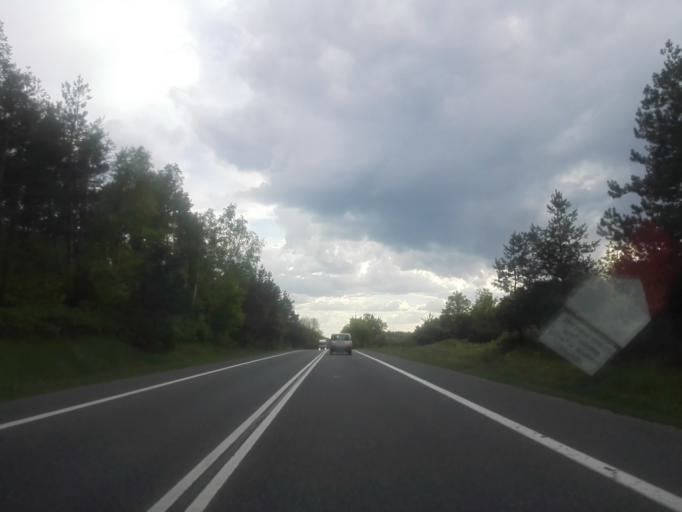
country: PL
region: Podlasie
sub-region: Powiat zambrowski
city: Szumowo
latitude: 52.8604
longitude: 22.0012
